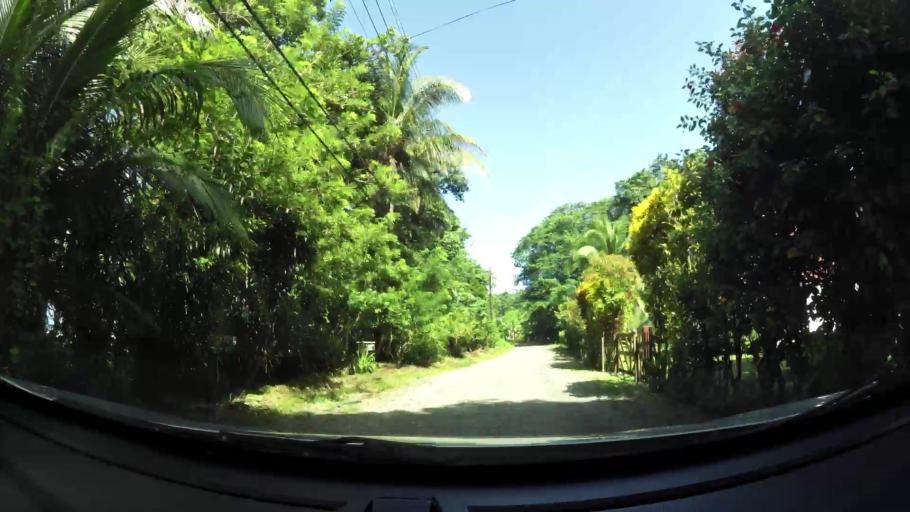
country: PA
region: Bocas del Toro
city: Barranco
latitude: 9.6408
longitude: -82.6896
